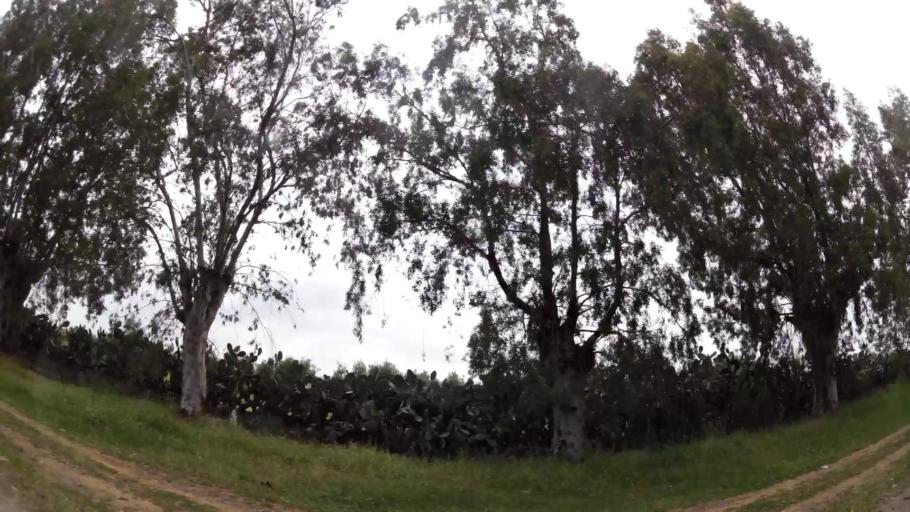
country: MA
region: Rabat-Sale-Zemmour-Zaer
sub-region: Khemisset
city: Tiflet
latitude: 33.8552
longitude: -6.2690
